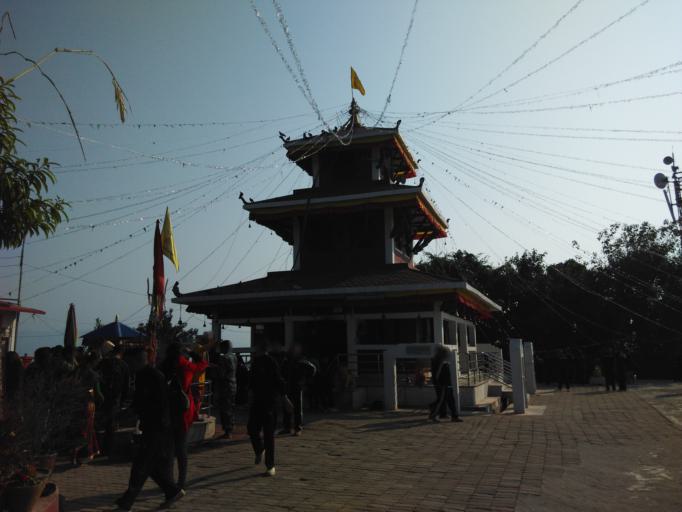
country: NP
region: Central Region
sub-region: Narayani Zone
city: Bharatpur
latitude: 27.7275
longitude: 84.4085
